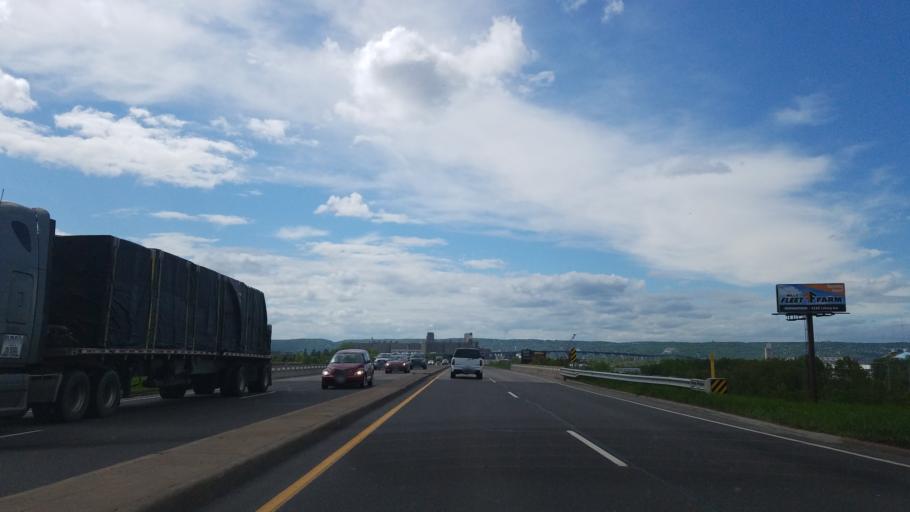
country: US
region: Wisconsin
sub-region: Douglas County
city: Superior
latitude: 46.7298
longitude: -92.0797
